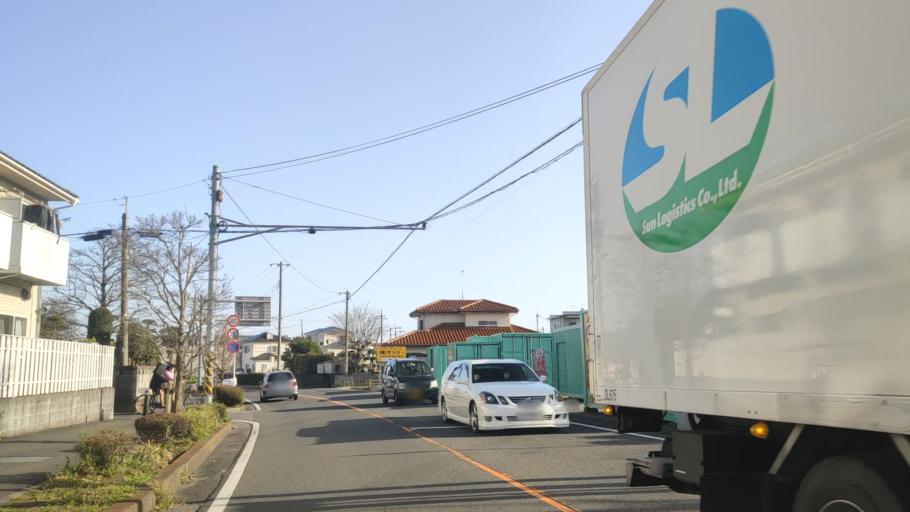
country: JP
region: Kanagawa
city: Zama
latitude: 35.5061
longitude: 139.3403
